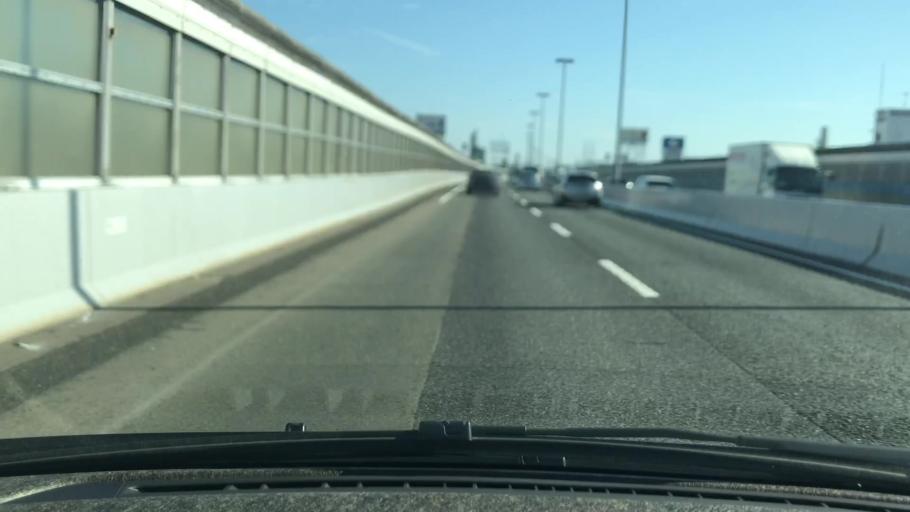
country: JP
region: Hyogo
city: Ashiya
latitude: 34.7112
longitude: 135.2559
